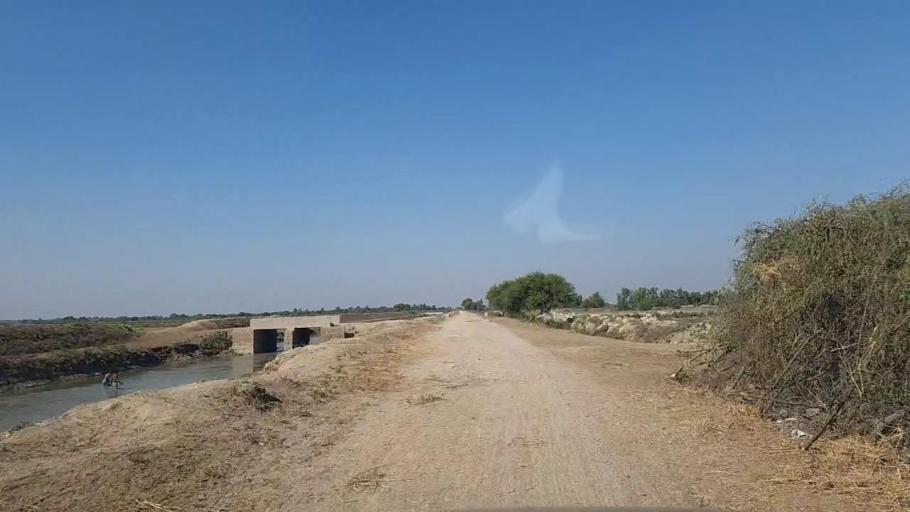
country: PK
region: Sindh
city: Mirpur Batoro
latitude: 24.7222
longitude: 68.2336
